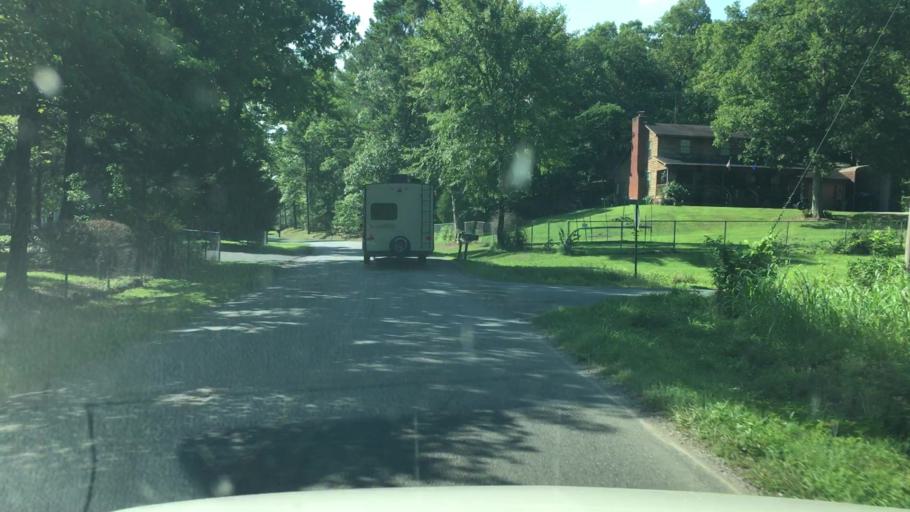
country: US
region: Arkansas
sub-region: Garland County
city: Piney
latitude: 34.5316
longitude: -93.3379
